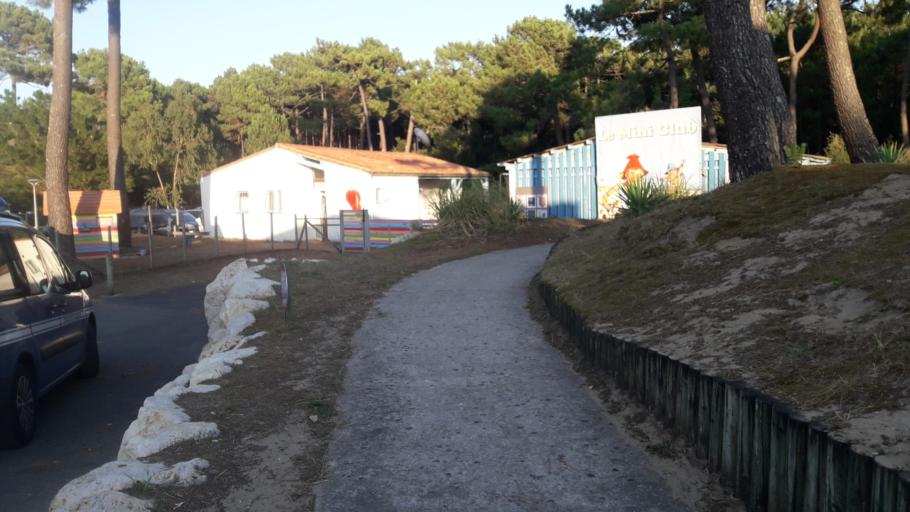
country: FR
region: Poitou-Charentes
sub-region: Departement de la Charente-Maritime
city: Les Mathes
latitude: 45.6885
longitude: -1.1887
